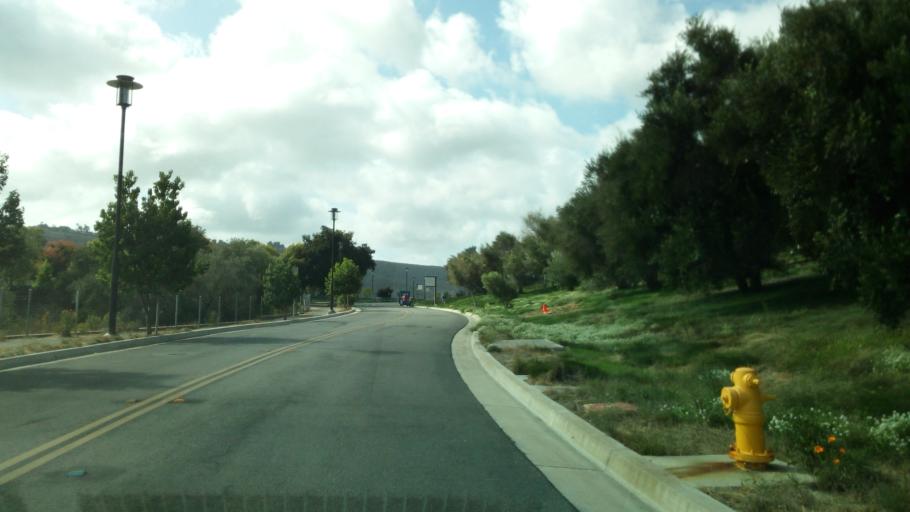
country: US
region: California
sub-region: Orange County
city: Aliso Viejo
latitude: 33.5516
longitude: -117.7359
